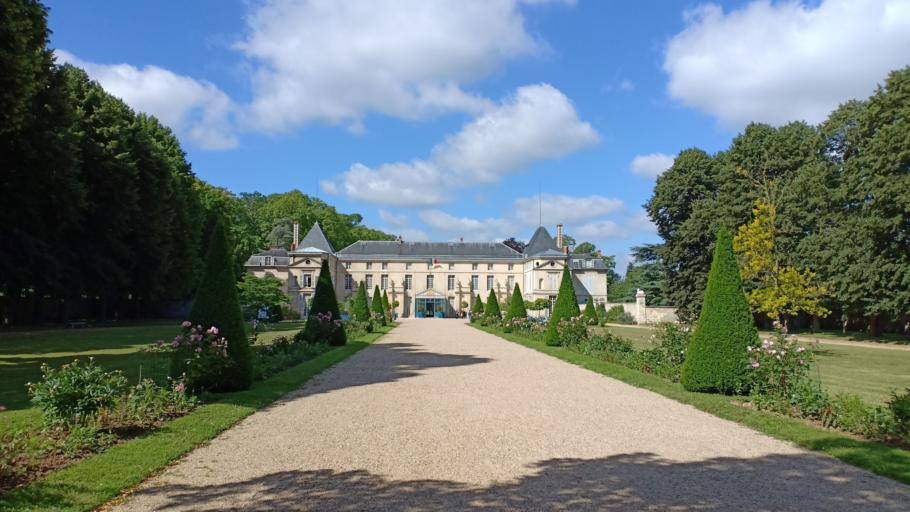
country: FR
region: Ile-de-France
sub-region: Departement des Yvelines
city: Chatou
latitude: 48.8714
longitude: 2.1684
